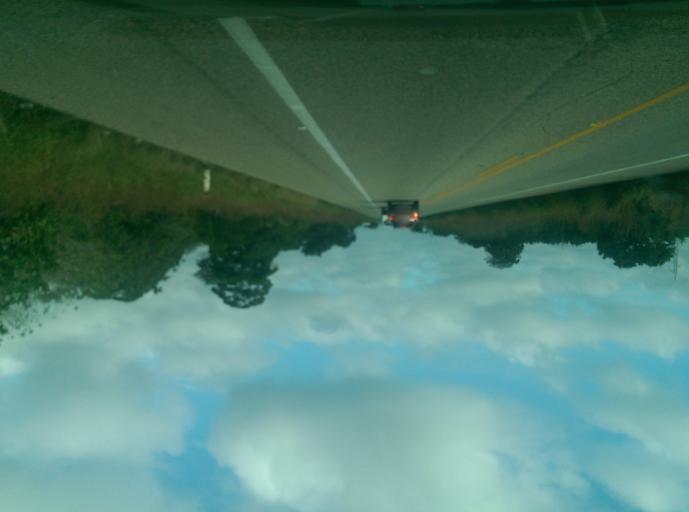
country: MX
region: Tabasco
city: Aquiles Serdan
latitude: 17.6998
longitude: -92.2542
